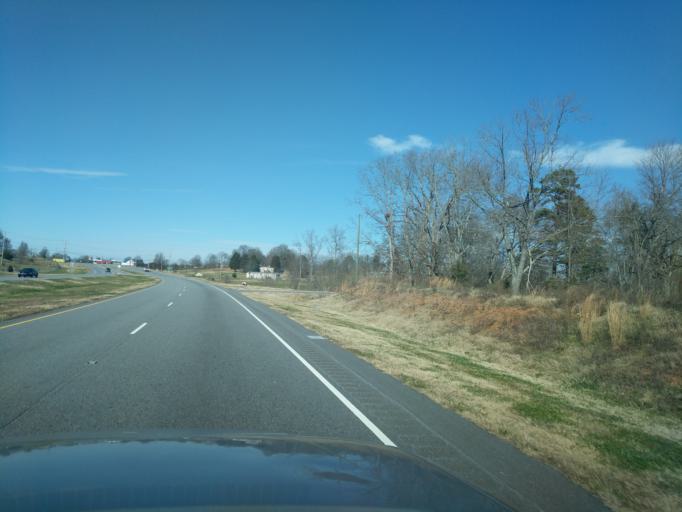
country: US
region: North Carolina
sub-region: Rutherford County
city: Forest City
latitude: 35.2319
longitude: -81.8448
